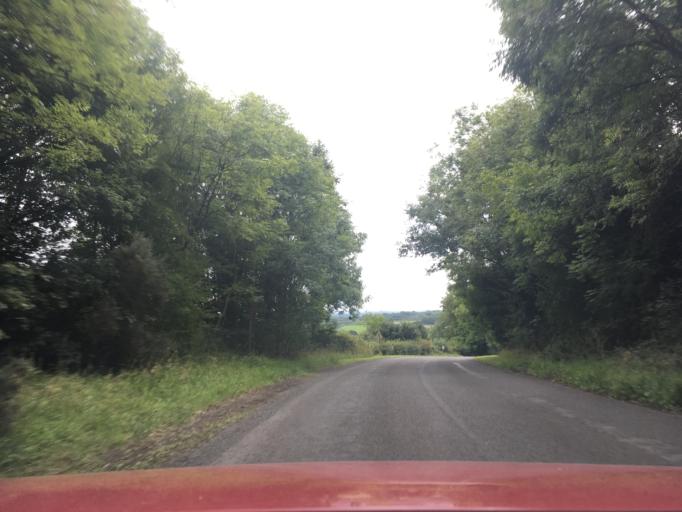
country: GB
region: England
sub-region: South Gloucestershire
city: Tytherington
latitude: 51.5851
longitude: -2.4983
